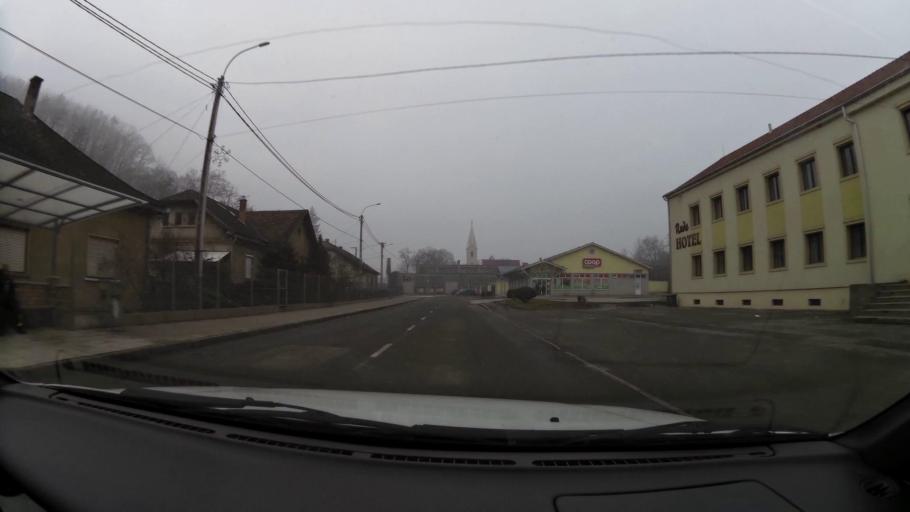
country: HU
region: Borsod-Abauj-Zemplen
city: Rudabanya
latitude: 48.3750
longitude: 20.6208
